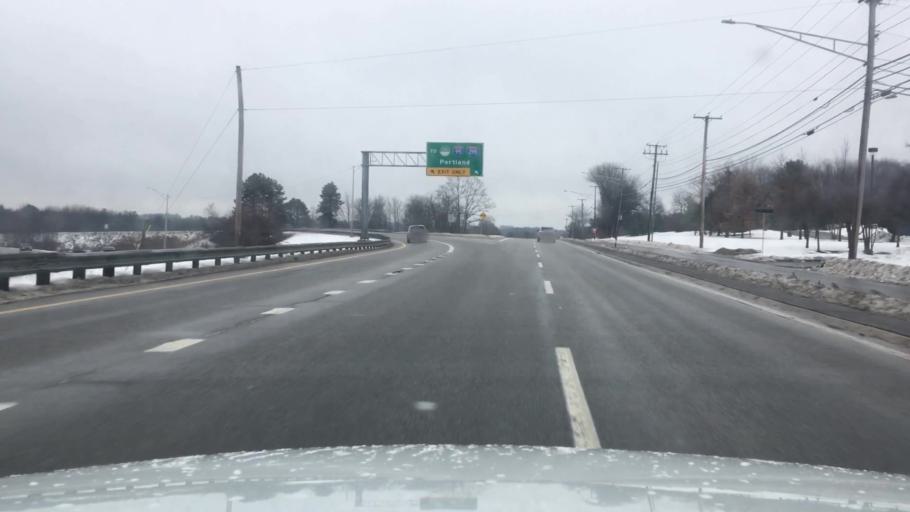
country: US
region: Maine
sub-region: Cumberland County
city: Scarborough
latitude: 43.6018
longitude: -70.3192
